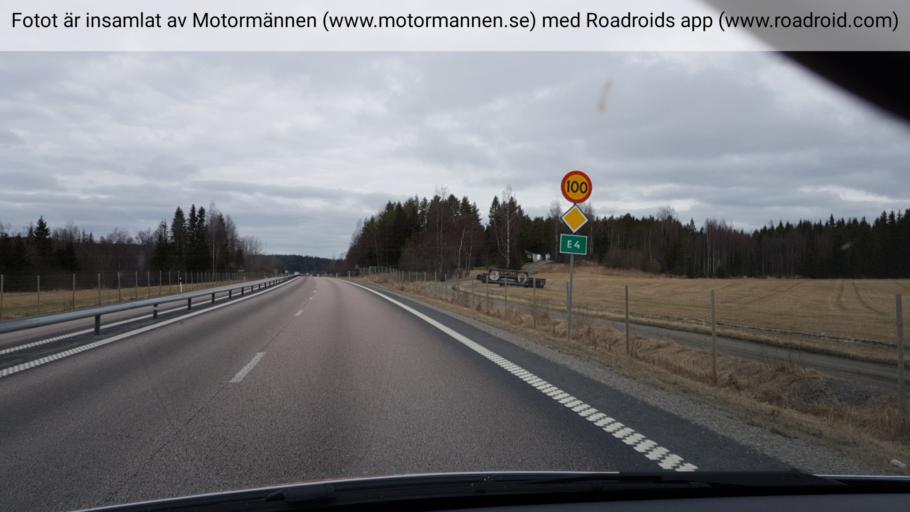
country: SE
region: Vaesternorrland
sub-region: OErnskoeldsviks Kommun
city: Ornskoldsvik
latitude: 63.3023
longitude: 18.8592
